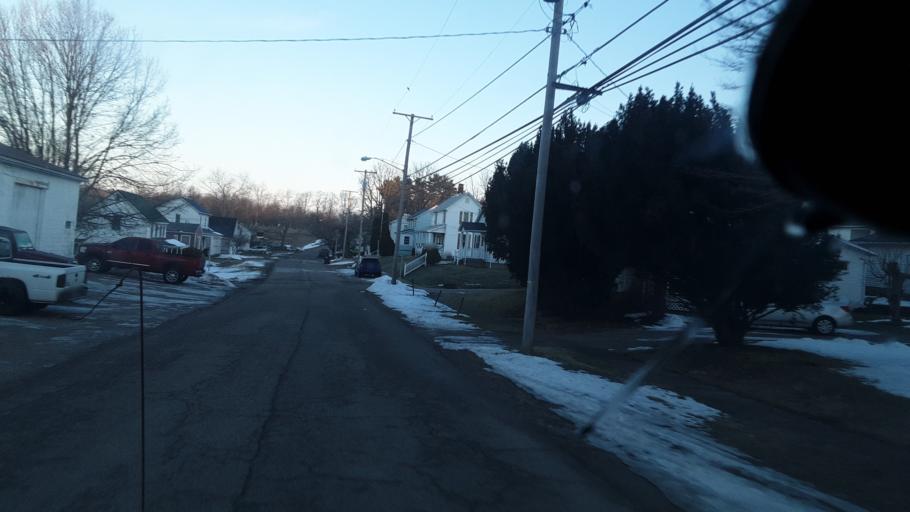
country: US
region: Ohio
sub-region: Perry County
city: Somerset
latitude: 39.8043
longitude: -82.3005
